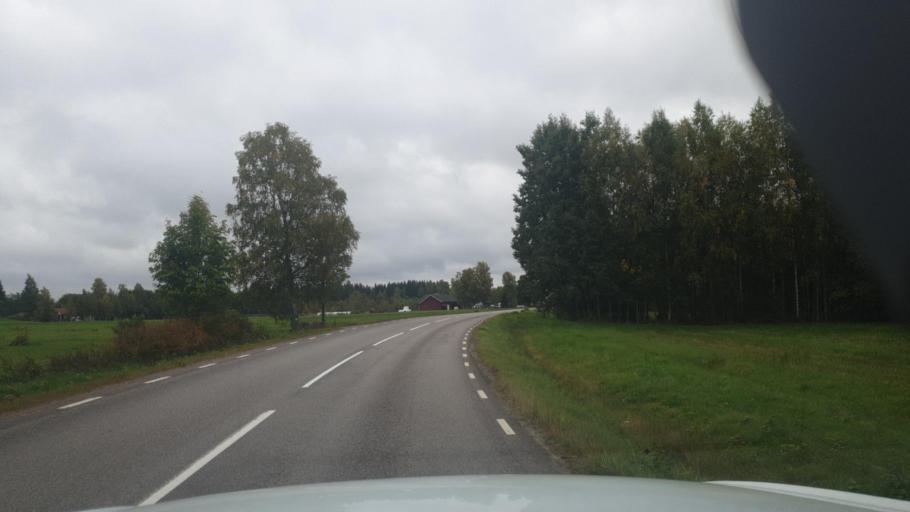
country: SE
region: Vaermland
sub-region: Sunne Kommun
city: Sunne
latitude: 59.7973
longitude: 13.0672
